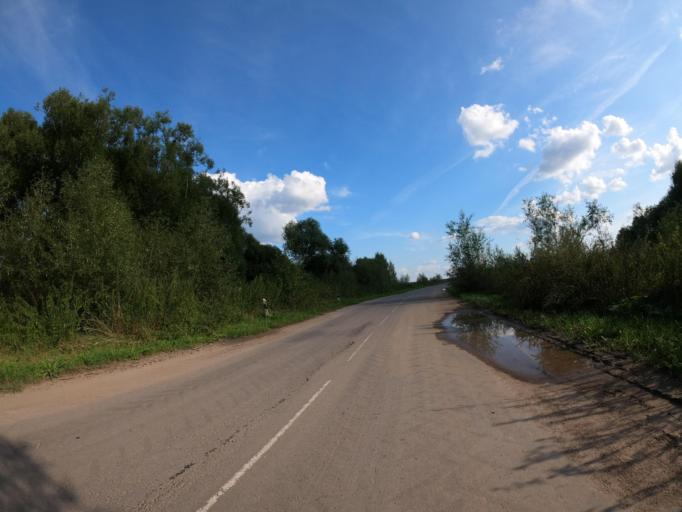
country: RU
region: Moskovskaya
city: Troitskoye
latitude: 55.2079
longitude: 38.4885
